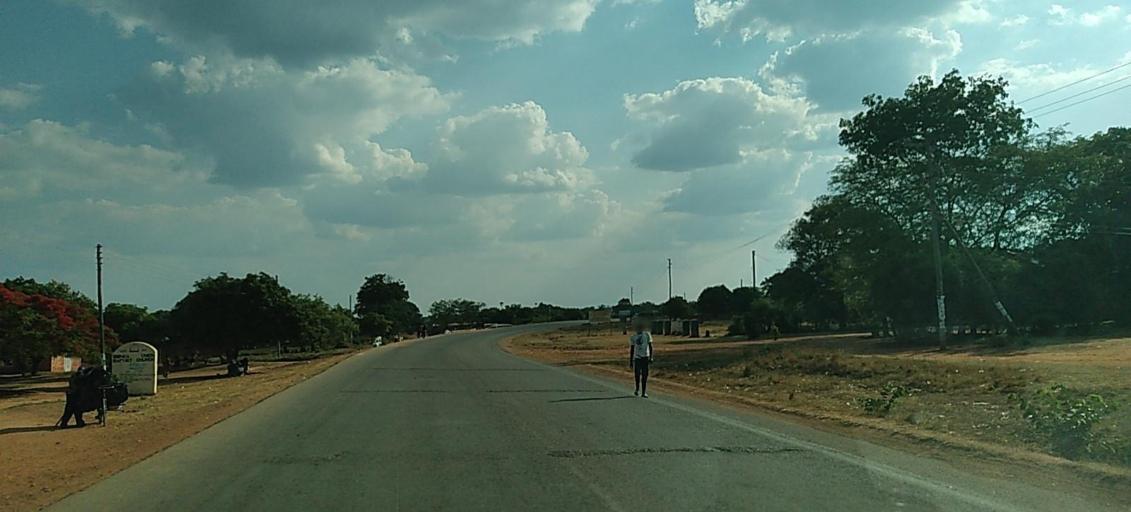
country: ZM
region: Copperbelt
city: Luanshya
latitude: -13.3600
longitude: 28.4140
